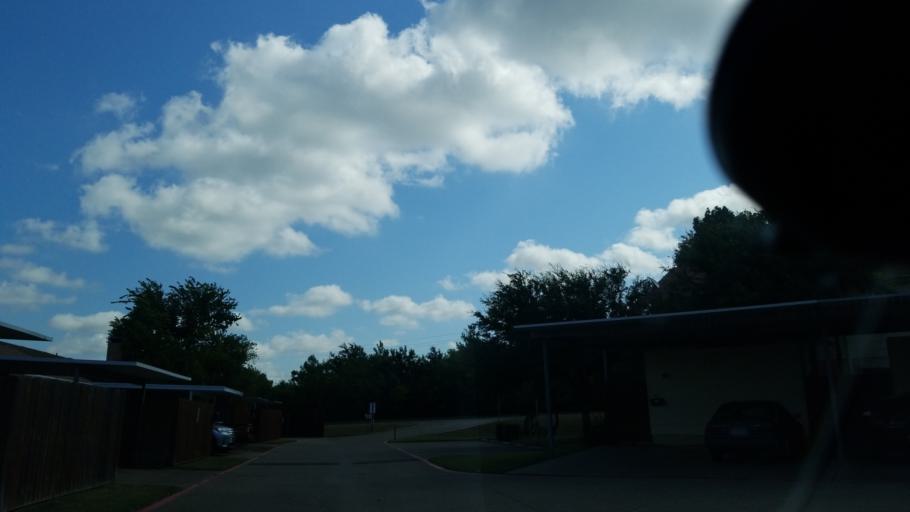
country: US
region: Texas
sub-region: Dallas County
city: Grand Prairie
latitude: 32.6959
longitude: -96.9862
